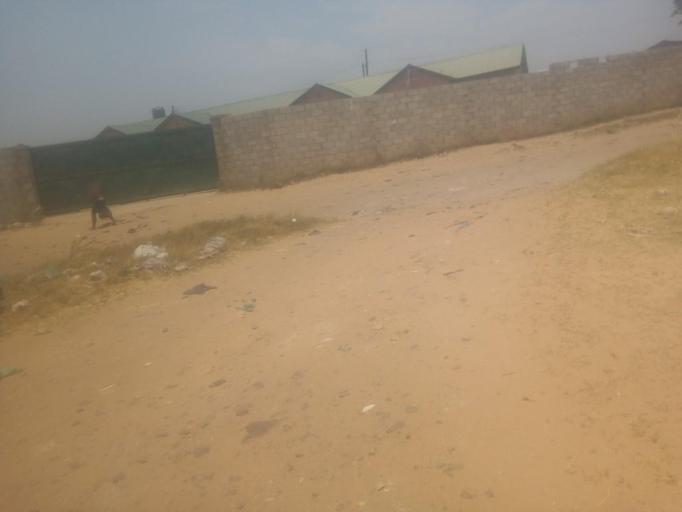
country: ZM
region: Lusaka
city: Lusaka
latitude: -15.4059
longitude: 28.3716
